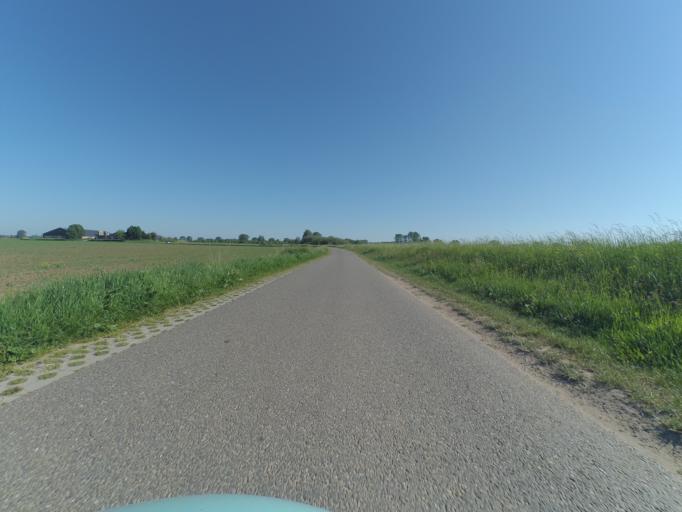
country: NL
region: Gelderland
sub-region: Gemeente Lochem
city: Gorssel
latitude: 52.2116
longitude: 6.1805
